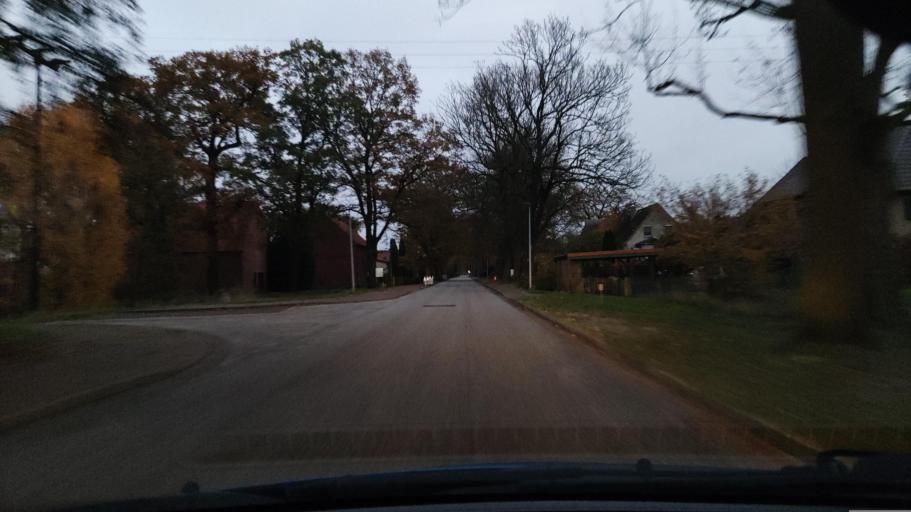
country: DE
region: Mecklenburg-Vorpommern
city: Neu Kaliss
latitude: 53.1795
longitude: 11.2818
